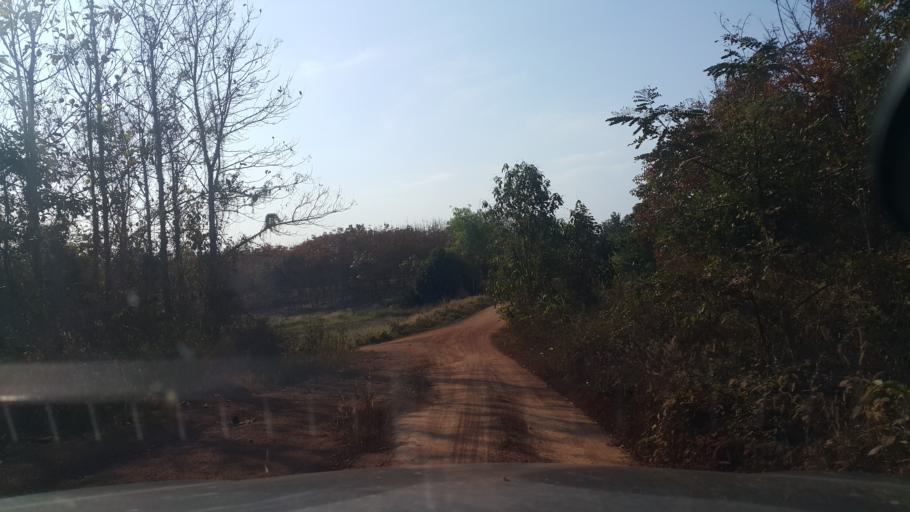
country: TH
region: Loei
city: Chiang Khan
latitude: 17.8236
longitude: 101.6170
